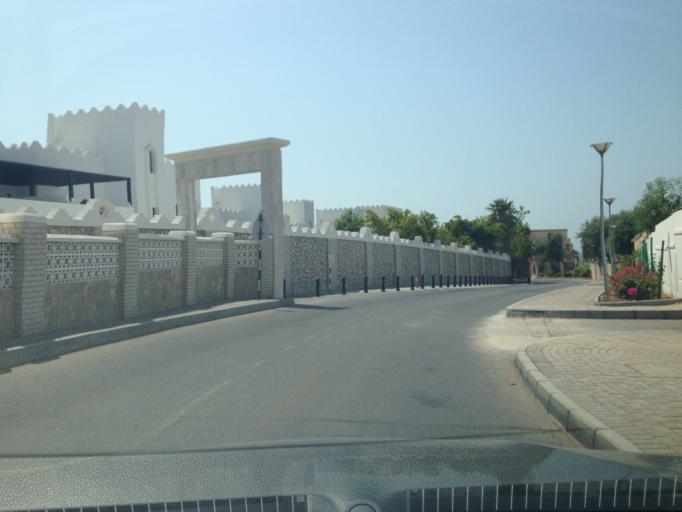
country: OM
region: Muhafazat Masqat
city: Muscat
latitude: 23.6304
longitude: 58.4856
